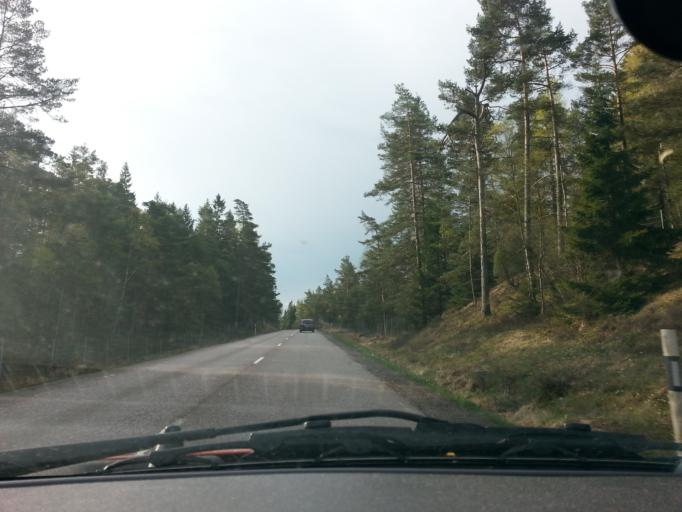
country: SE
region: Vaestra Goetaland
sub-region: Partille Kommun
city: Furulund
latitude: 57.6974
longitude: 12.1556
